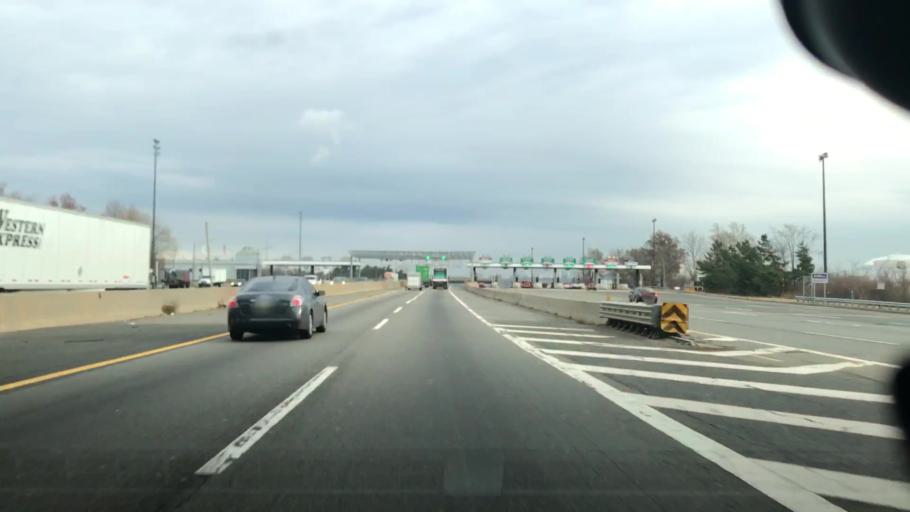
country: US
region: New Jersey
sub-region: Hudson County
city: Secaucus
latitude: 40.8103
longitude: -74.0619
